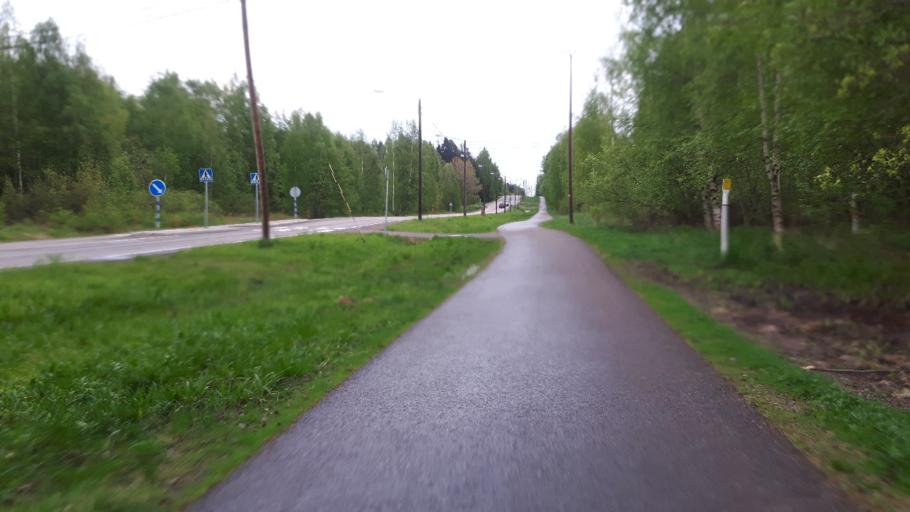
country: FI
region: Kymenlaakso
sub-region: Kotka-Hamina
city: Hamina
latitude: 60.5644
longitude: 27.1400
